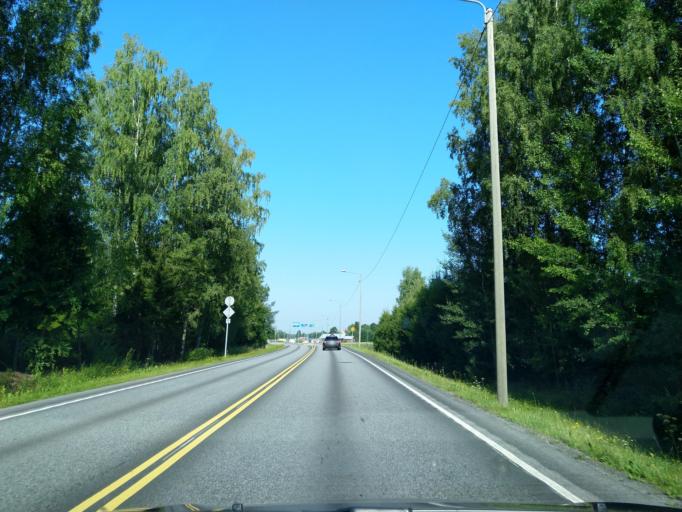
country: FI
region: Satakunta
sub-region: Pori
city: Huittinen
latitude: 61.1650
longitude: 22.7110
